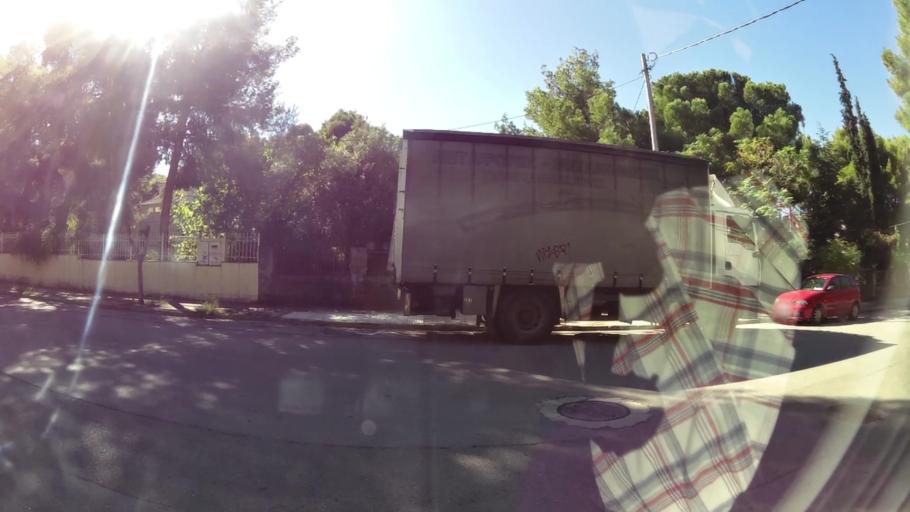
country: GR
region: Attica
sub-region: Nomarchia Athinas
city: Nea Erythraia
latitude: 38.0943
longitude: 23.7983
